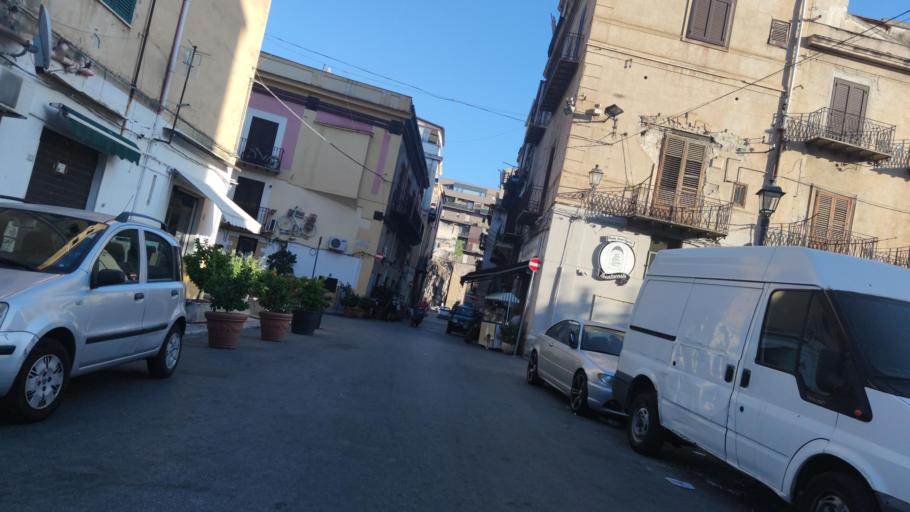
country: IT
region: Sicily
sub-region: Palermo
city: Palermo
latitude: 38.1105
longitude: 13.3614
